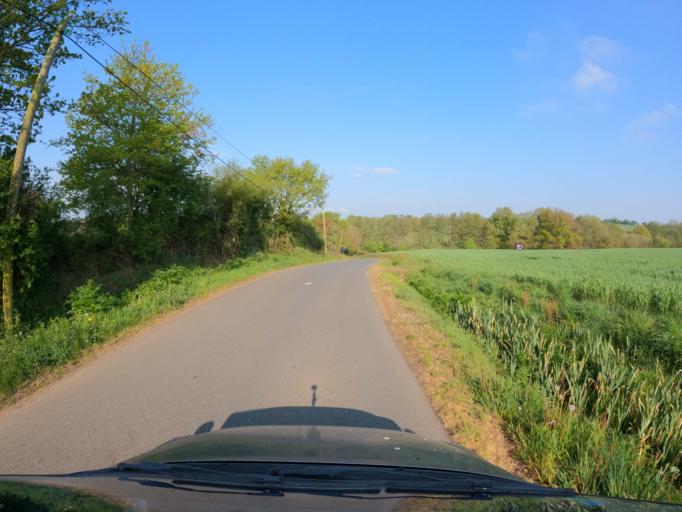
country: FR
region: Pays de la Loire
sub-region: Departement de Maine-et-Loire
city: La Seguiniere
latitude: 47.0678
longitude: -0.9580
